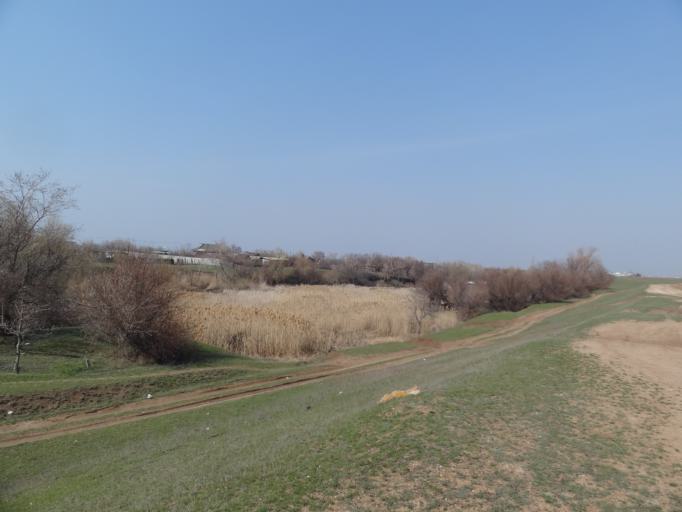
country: RU
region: Saratov
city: Privolzhskiy
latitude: 51.3077
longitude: 45.9661
